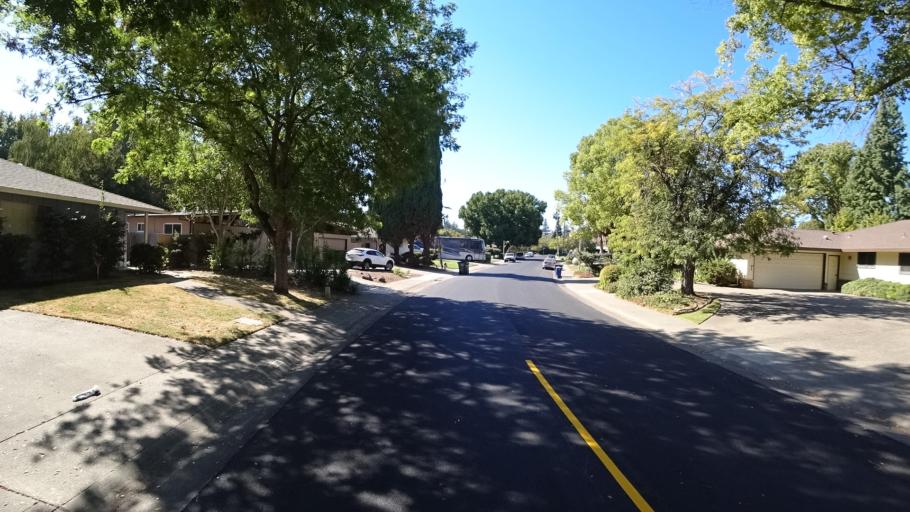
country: US
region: California
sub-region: Sacramento County
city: Parkway
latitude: 38.5073
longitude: -121.5237
